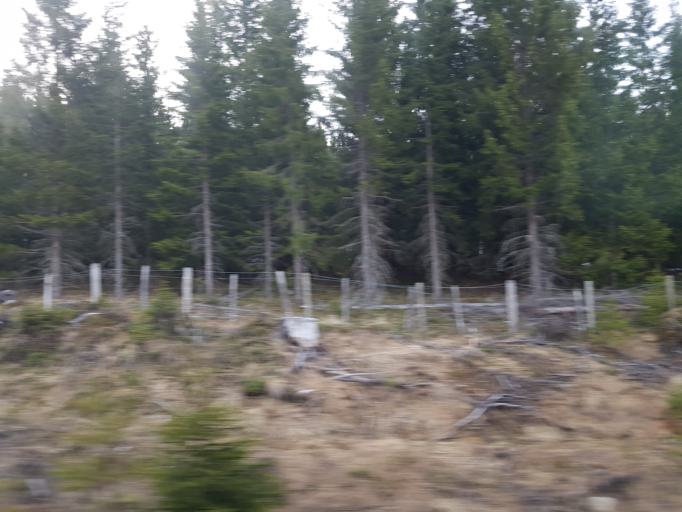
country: NO
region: Sor-Trondelag
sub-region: Rennebu
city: Berkak
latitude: 62.8641
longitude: 10.0263
